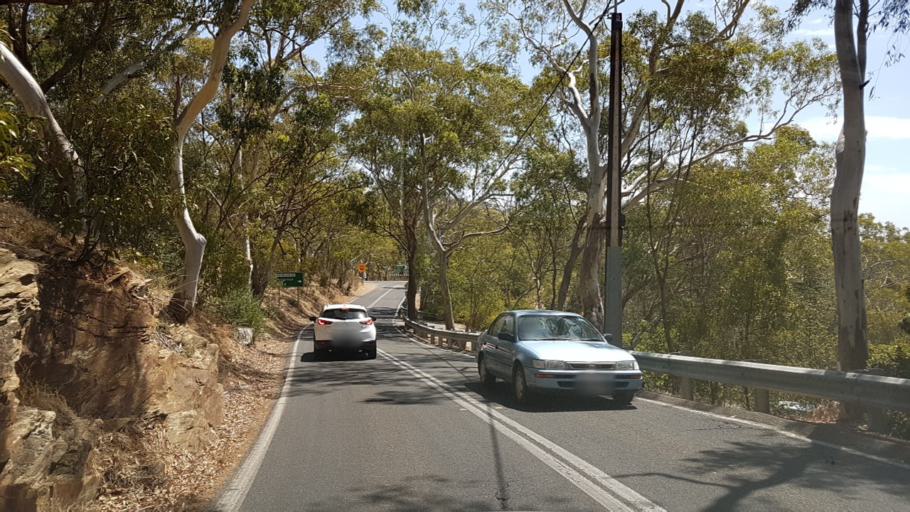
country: AU
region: South Australia
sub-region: Mitcham
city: Belair
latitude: -34.9930
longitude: 138.6267
